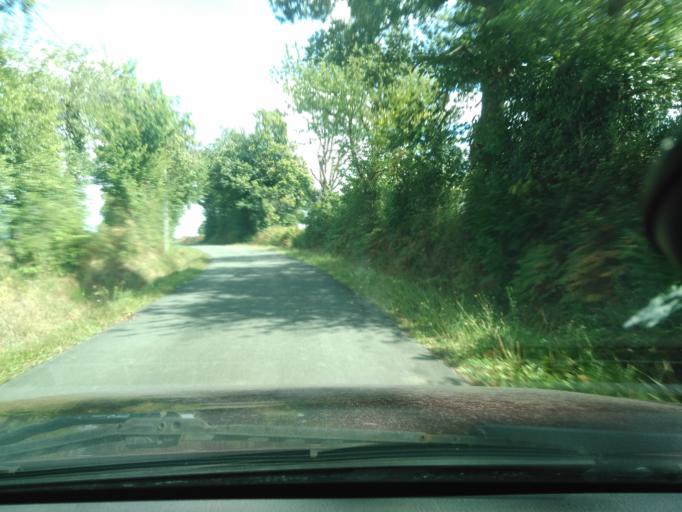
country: FR
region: Pays de la Loire
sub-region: Departement de la Vendee
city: Dompierre-sur-Yon
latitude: 46.7416
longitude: -1.3654
